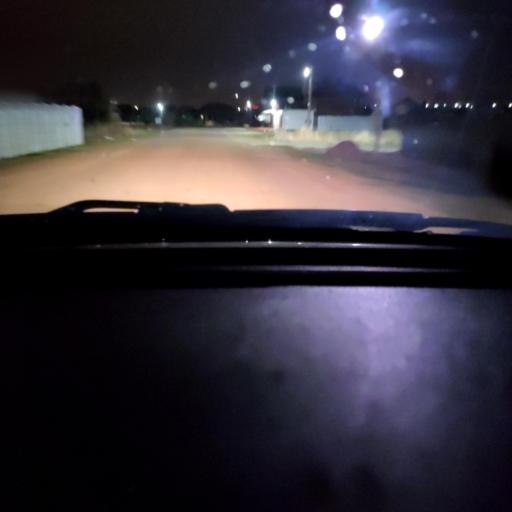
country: RU
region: Voronezj
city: Novaya Usman'
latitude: 51.5989
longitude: 39.3257
